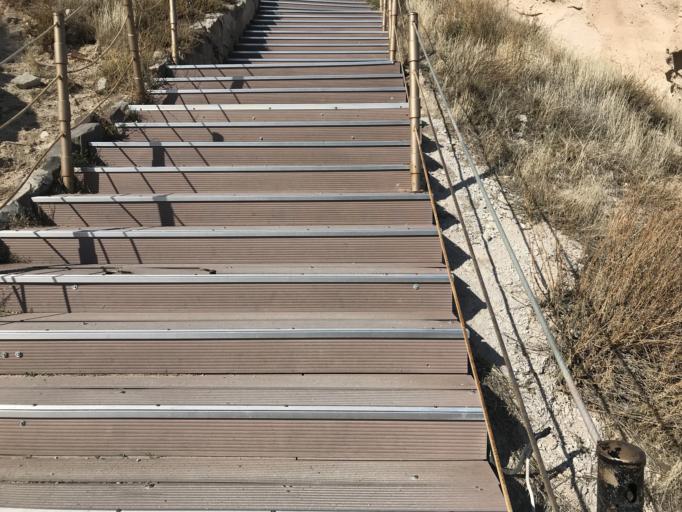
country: TR
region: Nevsehir
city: Goereme
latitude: 38.6304
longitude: 34.8059
